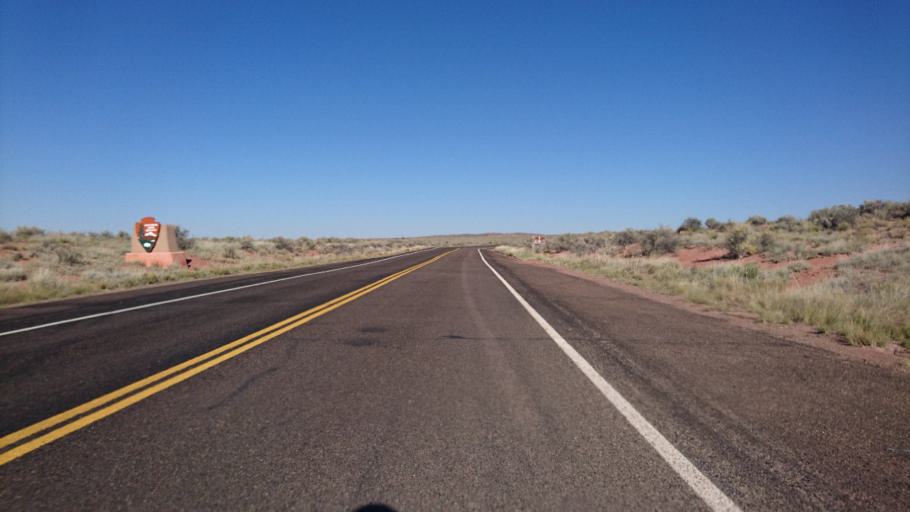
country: US
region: Arizona
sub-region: Navajo County
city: Holbrook
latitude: 35.0622
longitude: -109.7836
